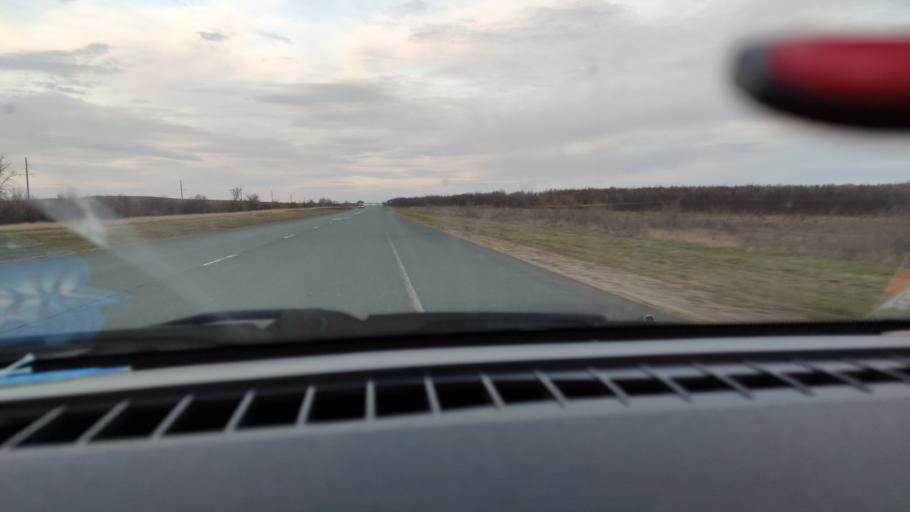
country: RU
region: Saratov
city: Yelshanka
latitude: 51.8274
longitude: 46.2706
